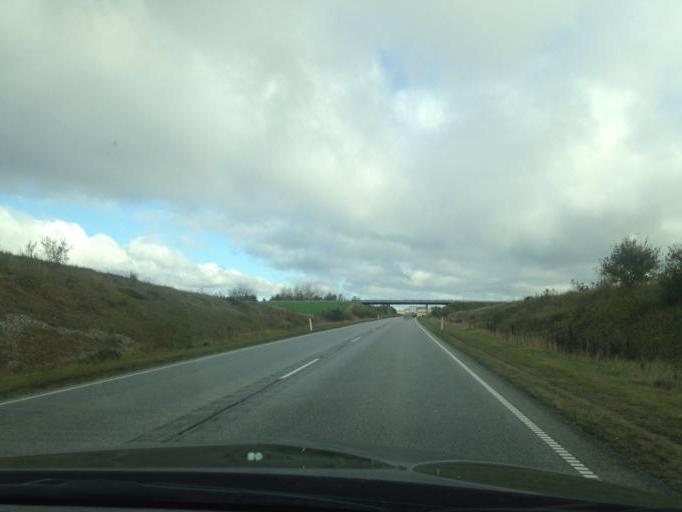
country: DK
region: South Denmark
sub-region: Vejle Kommune
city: Give
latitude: 55.8323
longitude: 9.2610
